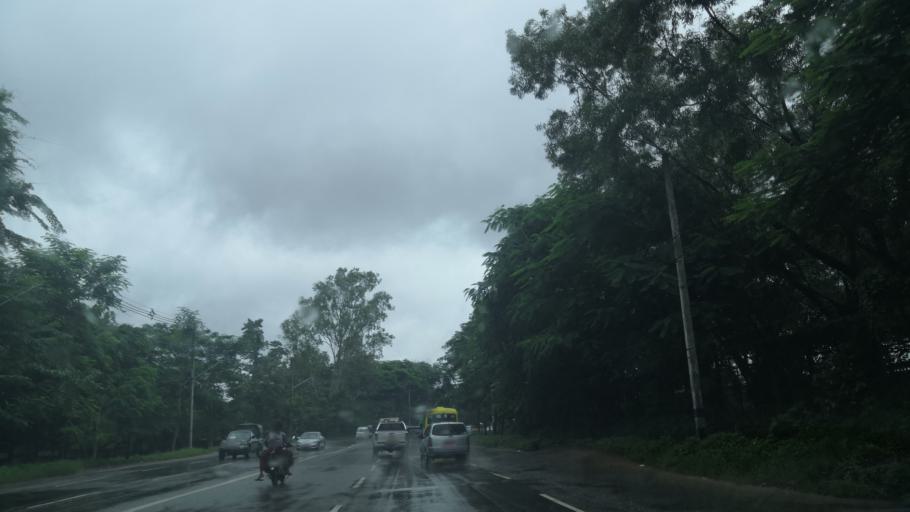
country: MM
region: Yangon
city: Yangon
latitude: 16.9029
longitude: 96.1264
